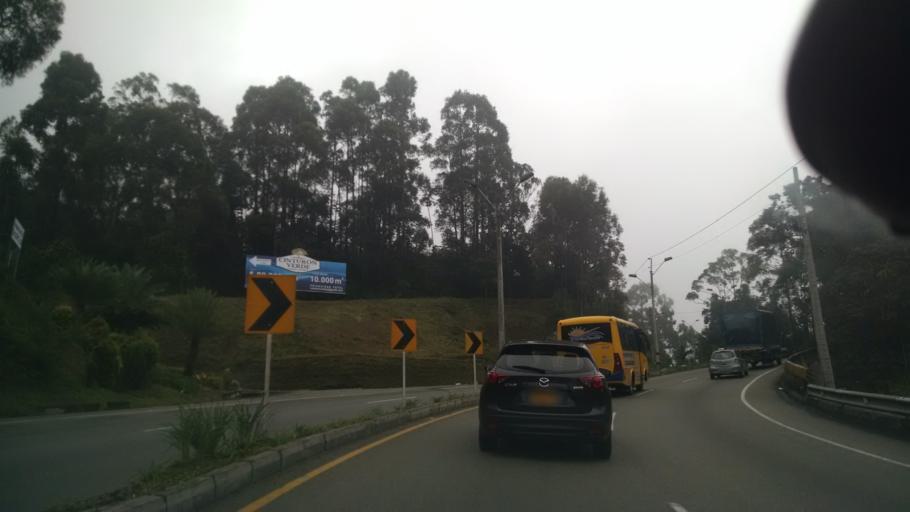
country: CO
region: Antioquia
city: Envigado
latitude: 6.1994
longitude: -75.5464
